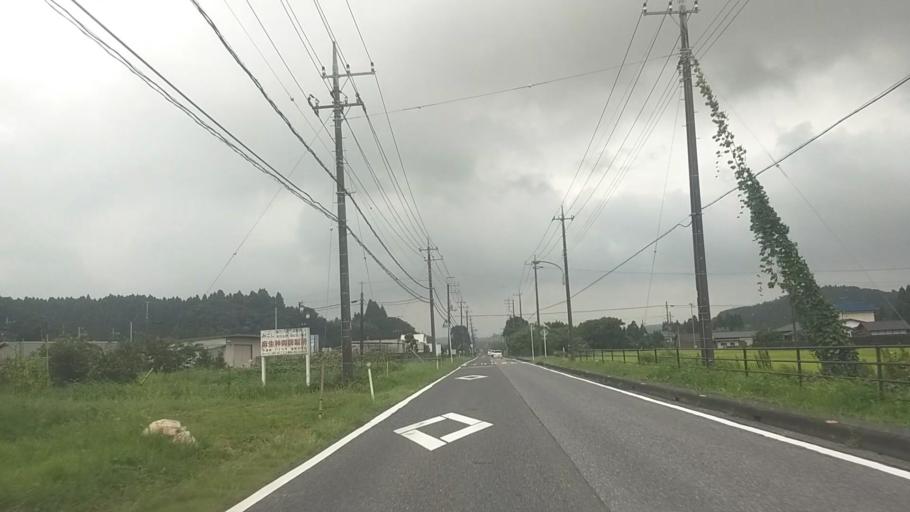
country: JP
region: Chiba
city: Ohara
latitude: 35.2850
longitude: 140.2692
